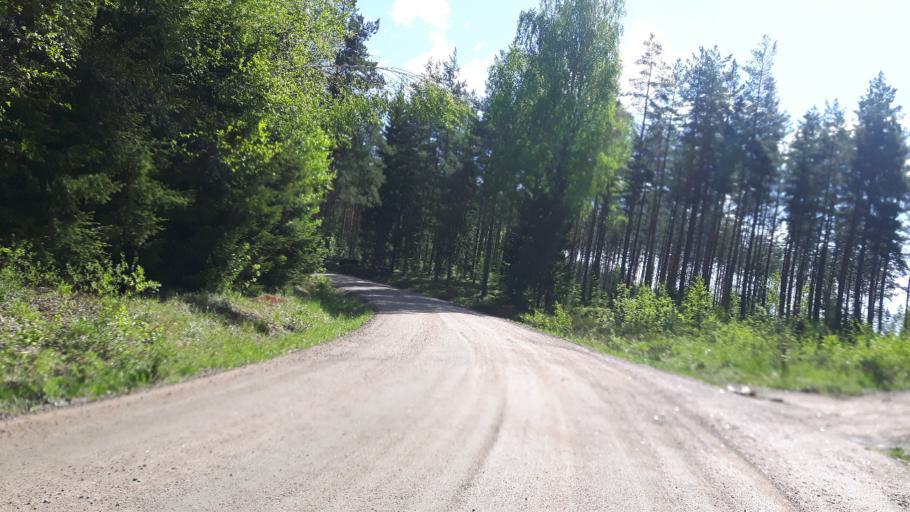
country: FI
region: Kymenlaakso
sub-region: Kotka-Hamina
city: Hamina
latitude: 60.5239
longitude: 27.2772
